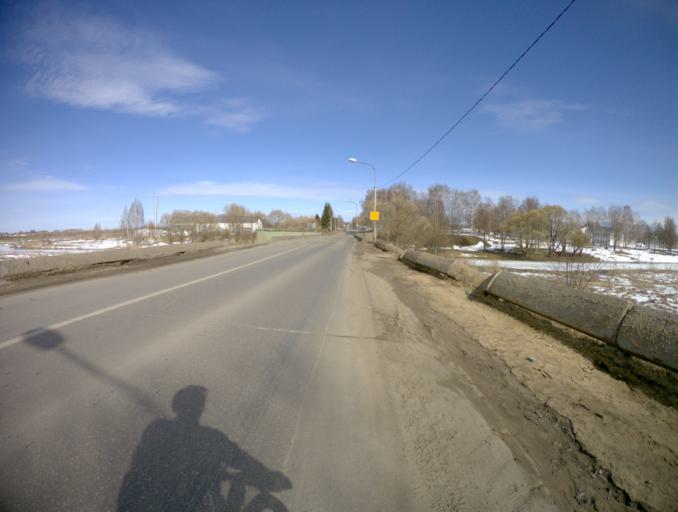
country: RU
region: Vladimir
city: Suzdal'
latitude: 56.4310
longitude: 40.4192
